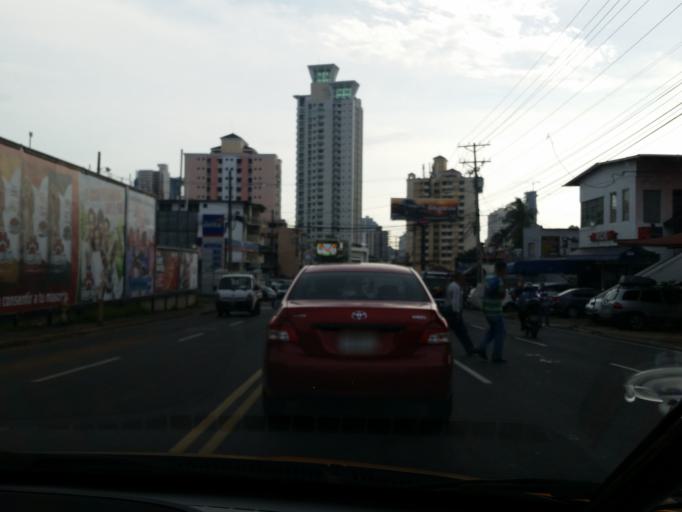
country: PA
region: Panama
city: Panama
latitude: 8.9949
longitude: -79.5150
